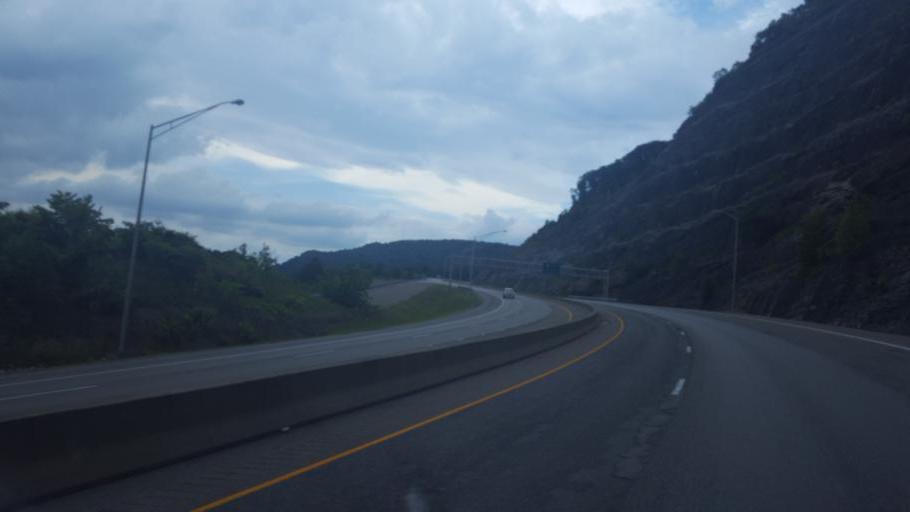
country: US
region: Kentucky
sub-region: Letcher County
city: Jenkins
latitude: 37.1567
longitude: -82.6463
